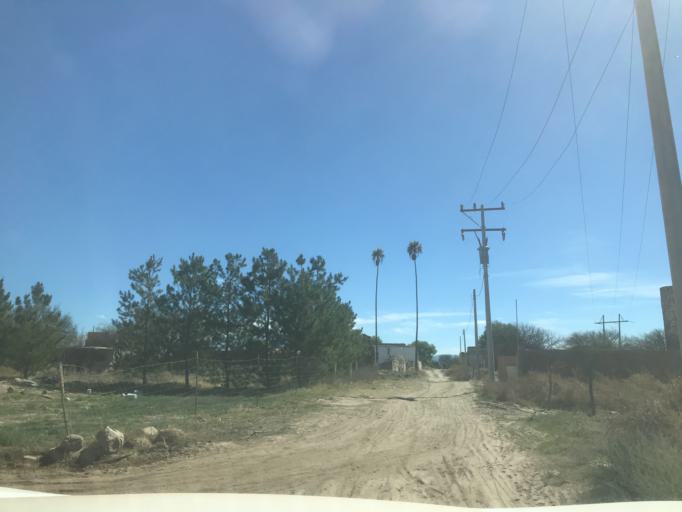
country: MX
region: Durango
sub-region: Durango
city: Sebastian Lerdo de Tejada
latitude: 23.9747
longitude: -104.6171
